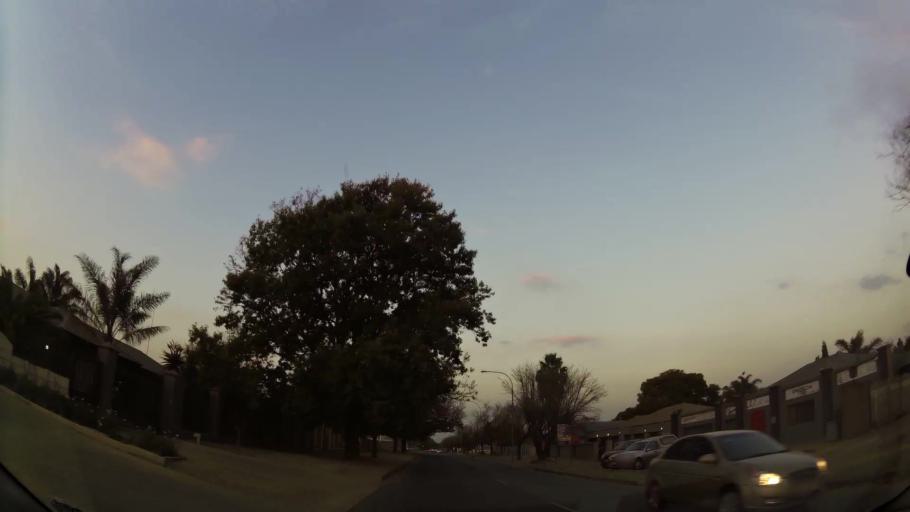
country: ZA
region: Gauteng
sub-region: Ekurhuleni Metropolitan Municipality
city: Benoni
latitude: -26.1641
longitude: 28.3193
